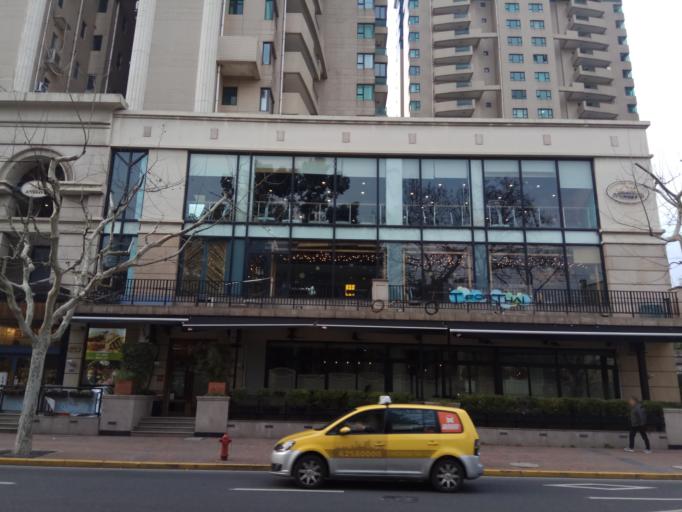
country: CN
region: Shanghai Shi
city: Xuhui
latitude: 31.2107
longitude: 121.4414
